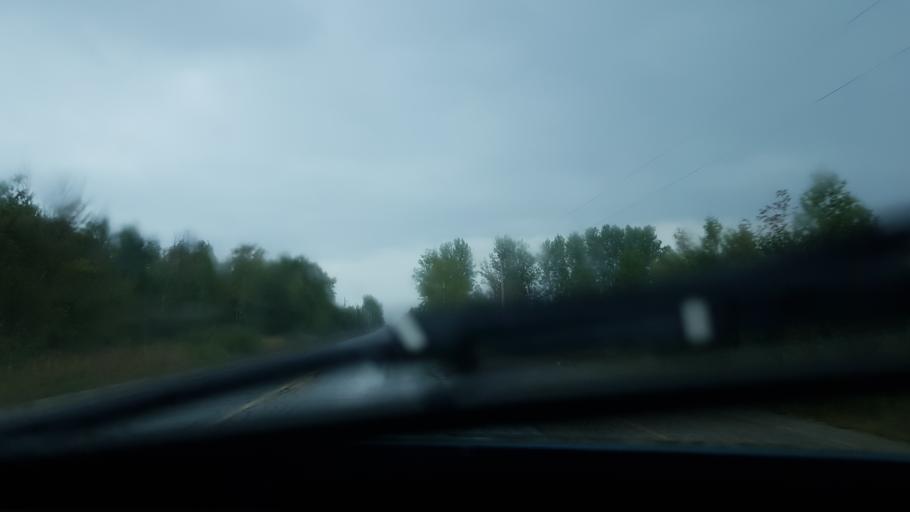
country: CA
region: Ontario
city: Omemee
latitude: 44.3901
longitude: -78.5552
